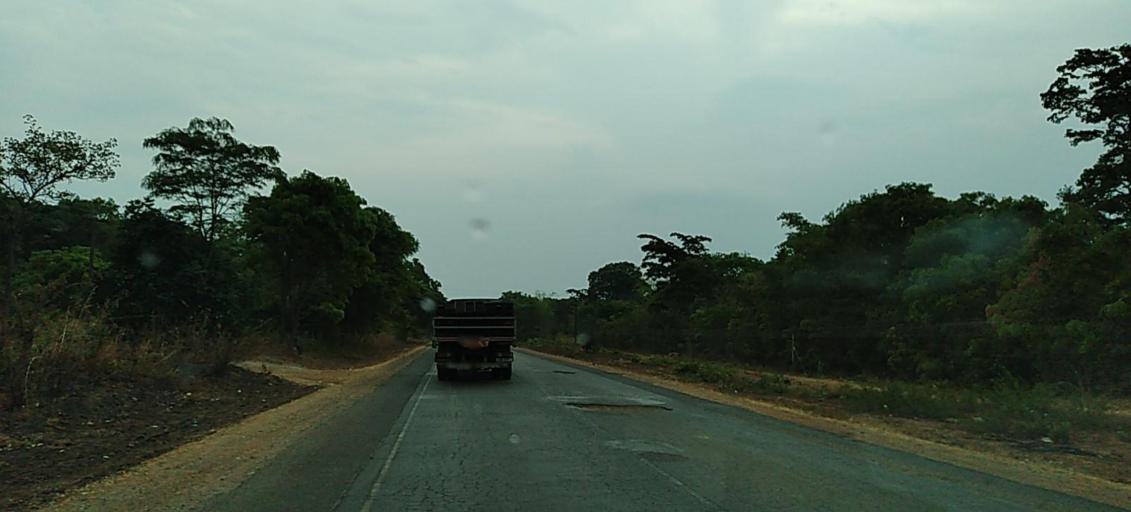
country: ZM
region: Copperbelt
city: Luanshya
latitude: -13.0610
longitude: 28.4569
